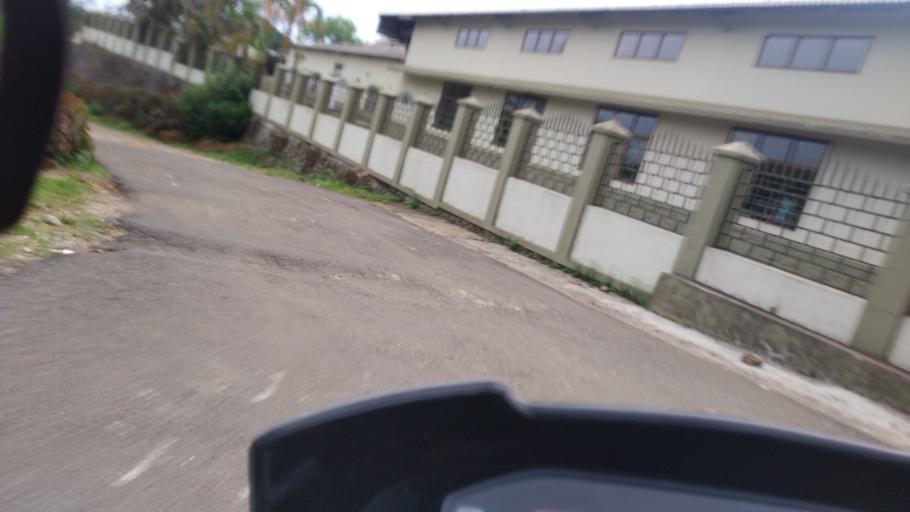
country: IN
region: Tamil Nadu
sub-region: Theni
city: Gudalur
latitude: 9.5420
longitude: 77.0410
